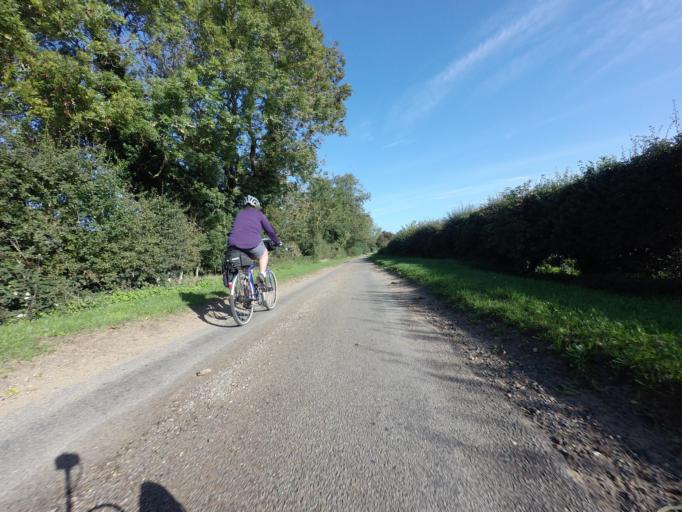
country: GB
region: England
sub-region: Norfolk
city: Dersingham
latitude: 52.8220
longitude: 0.6688
